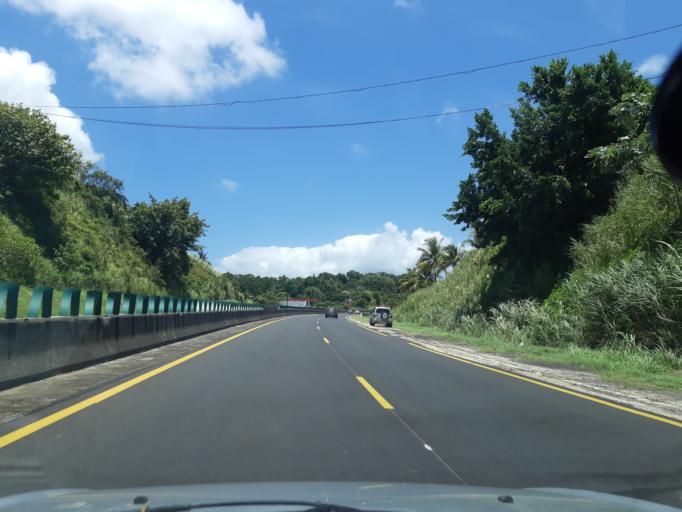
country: GP
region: Guadeloupe
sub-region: Guadeloupe
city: Petit-Bourg
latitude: 16.1849
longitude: -61.6062
